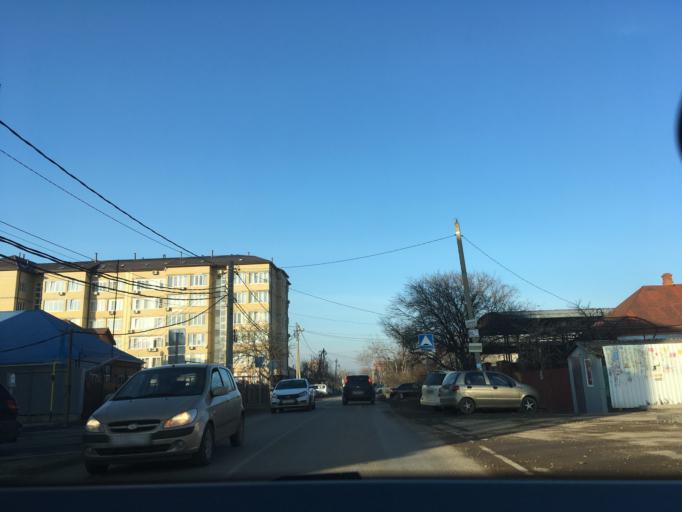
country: RU
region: Krasnodarskiy
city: Krasnodar
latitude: 45.0754
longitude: 39.0210
